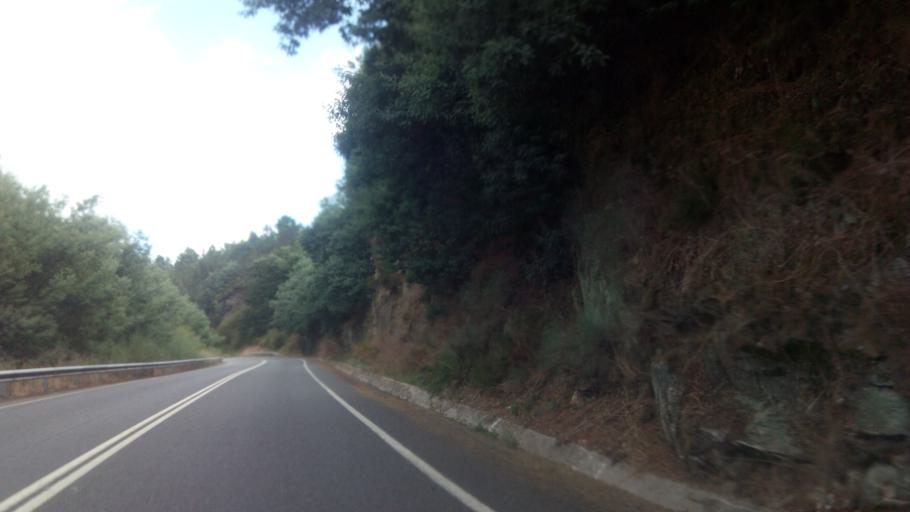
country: ES
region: Galicia
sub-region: Provincia de Ourense
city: Coles
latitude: 42.4011
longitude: -7.7993
